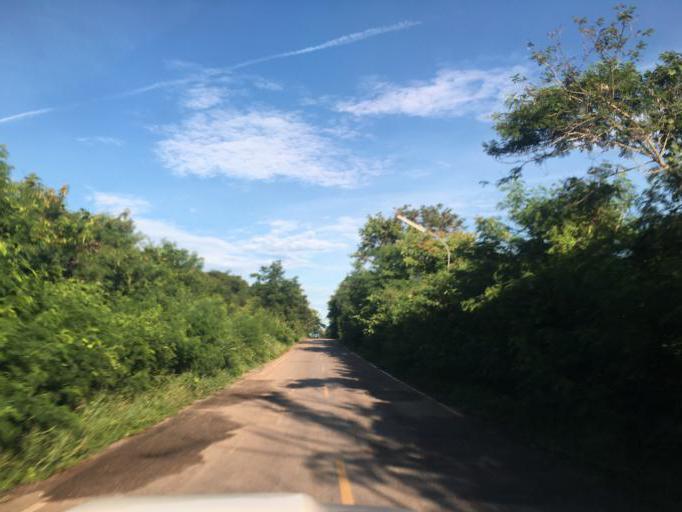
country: TH
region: Changwat Udon Thani
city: Kut Chap
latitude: 17.3801
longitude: 102.6013
